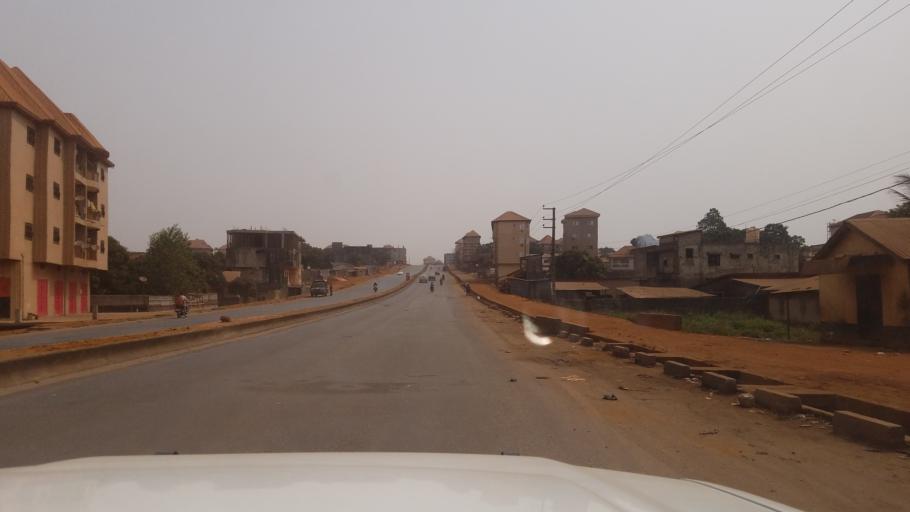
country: GN
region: Kindia
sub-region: Prefecture de Dubreka
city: Dubreka
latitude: 9.6723
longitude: -13.5529
